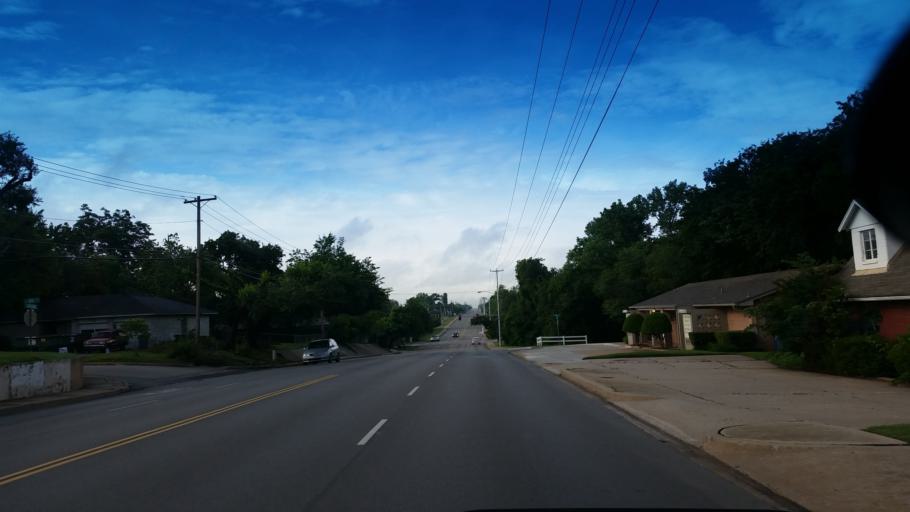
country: US
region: Oklahoma
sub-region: Oklahoma County
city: Edmond
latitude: 35.6472
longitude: -97.4782
